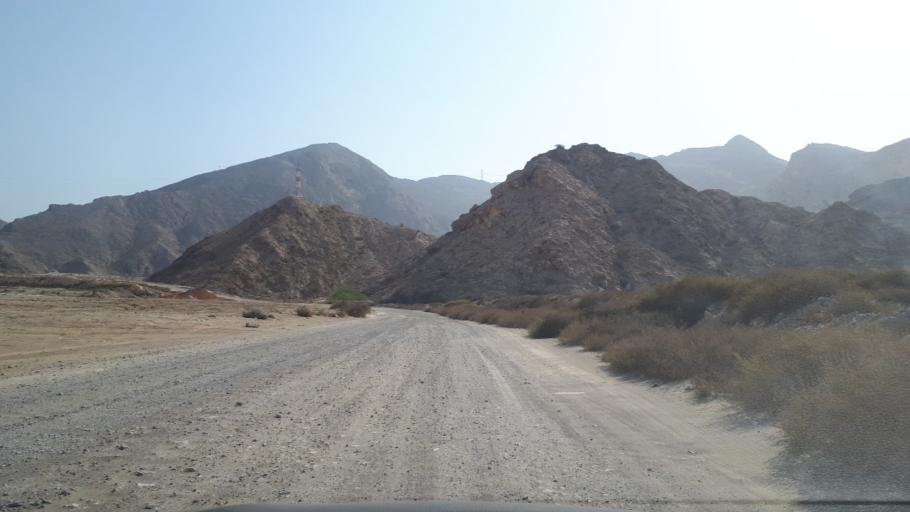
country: OM
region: Muhafazat Masqat
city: Muscat
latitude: 23.5377
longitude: 58.6529
